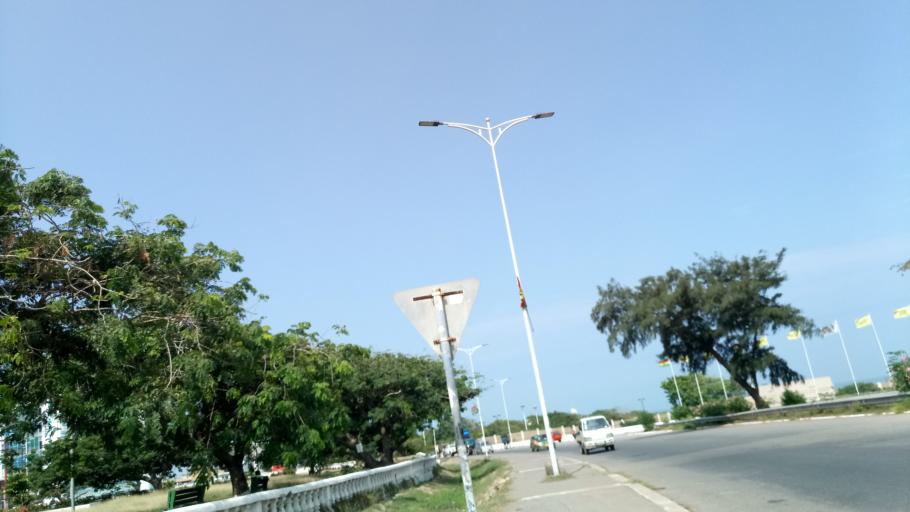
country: GH
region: Greater Accra
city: Accra
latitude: 5.5495
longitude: -0.1925
